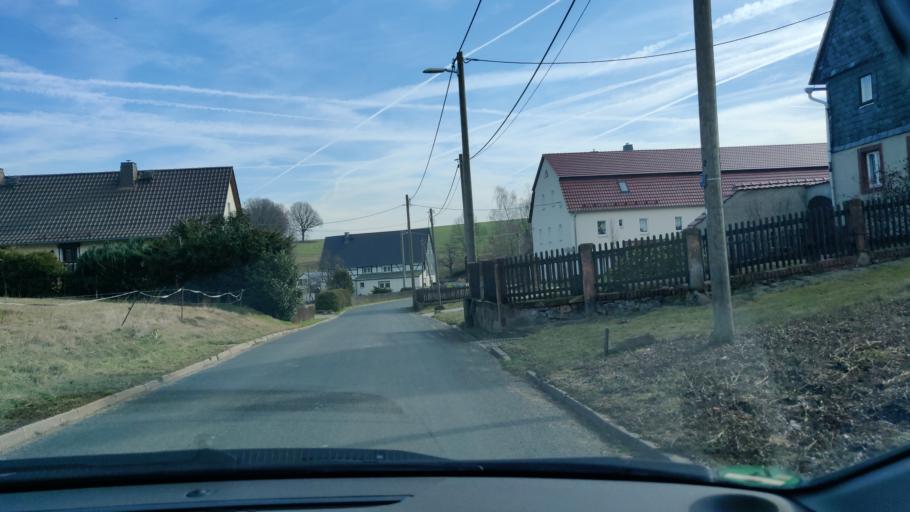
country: DE
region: Saxony
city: Konigsfeld
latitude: 51.0677
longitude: 12.7755
